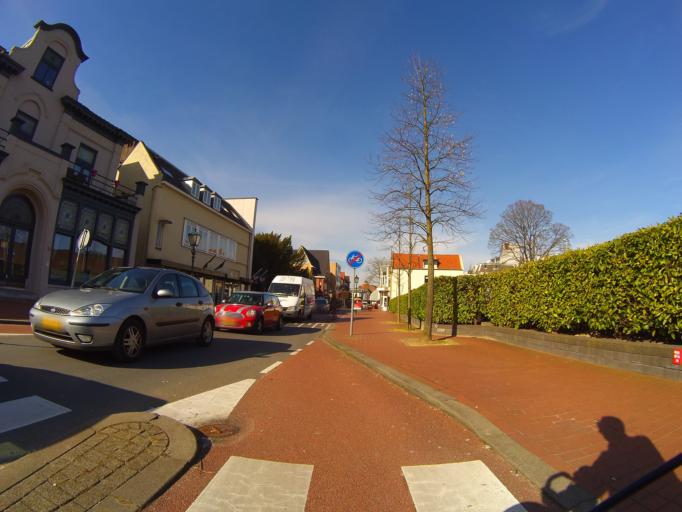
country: NL
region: North Holland
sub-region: Gemeente Bussum
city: Bussum
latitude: 52.2735
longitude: 5.1629
